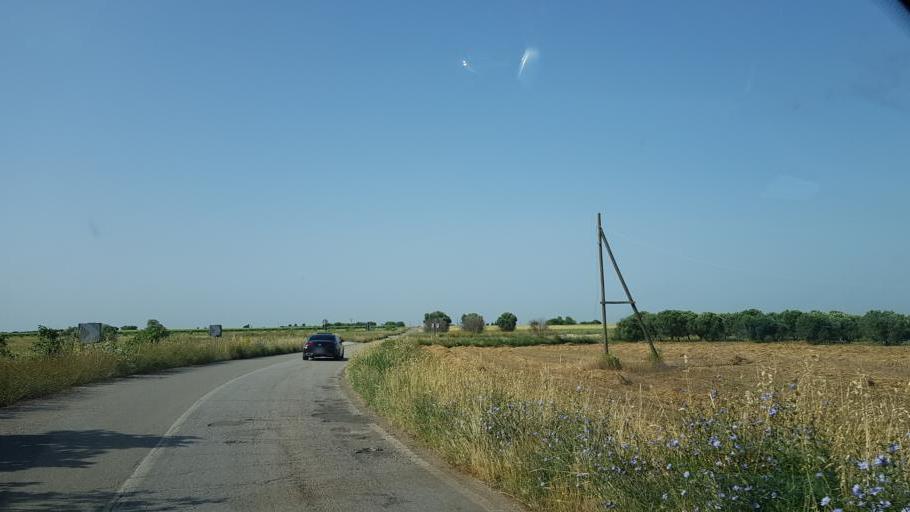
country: IT
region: Apulia
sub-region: Provincia di Brindisi
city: San Pancrazio Salentino
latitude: 40.4421
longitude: 17.8410
